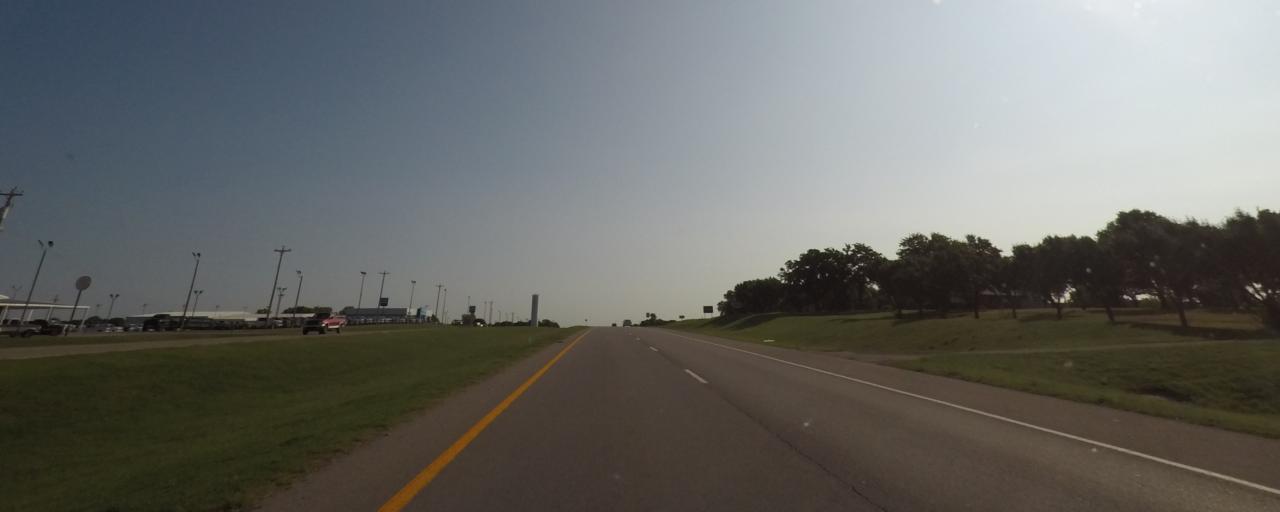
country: US
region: Oklahoma
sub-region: McClain County
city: Blanchard
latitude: 35.1472
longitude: -97.6394
